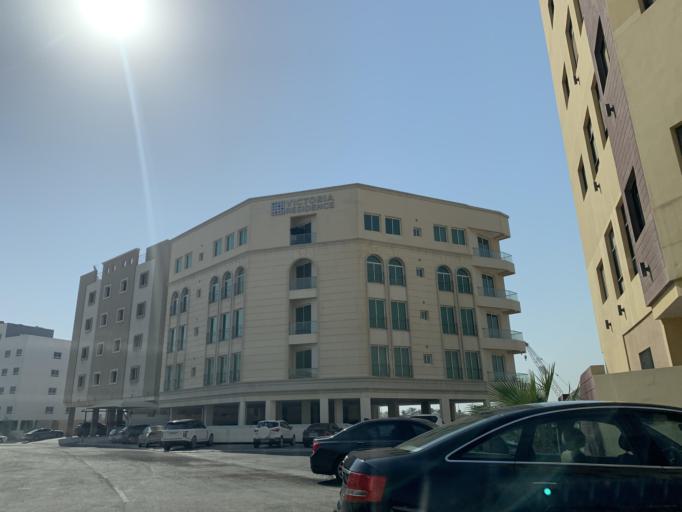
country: BH
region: Northern
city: Madinat `Isa
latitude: 26.1936
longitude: 50.5140
